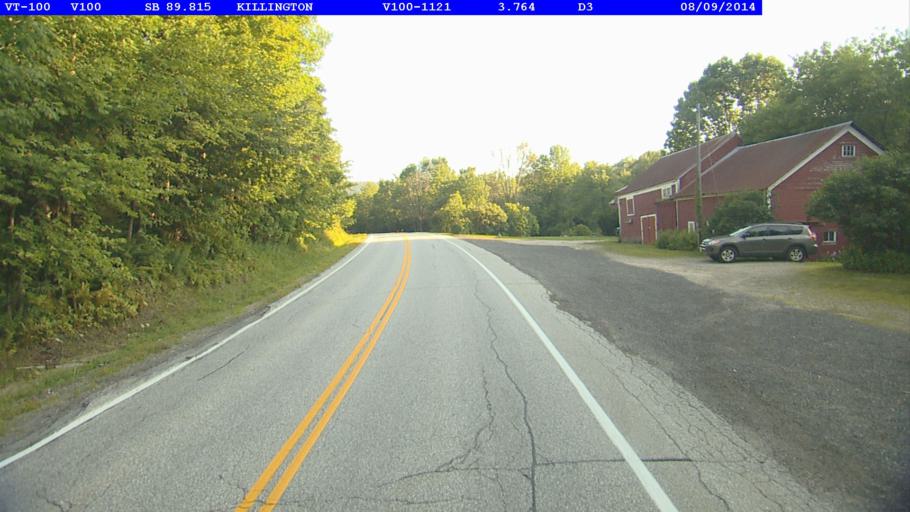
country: US
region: Vermont
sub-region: Rutland County
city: Rutland
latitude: 43.7154
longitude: -72.8269
